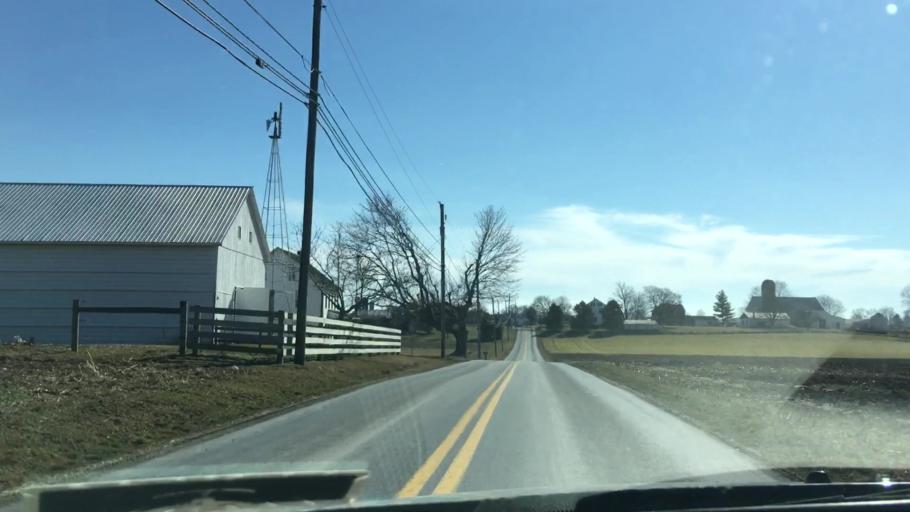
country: US
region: Pennsylvania
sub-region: Lancaster County
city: New Holland
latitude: 40.1321
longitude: -76.1319
